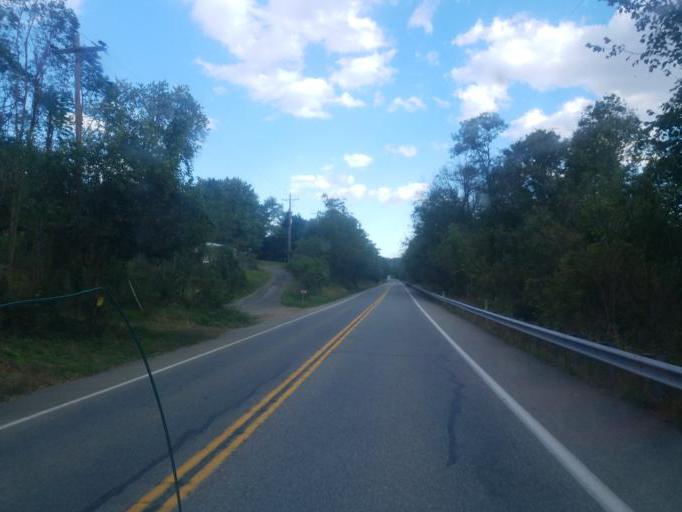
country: US
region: Pennsylvania
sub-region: Lancaster County
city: Bainbridge
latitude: 40.1197
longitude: -76.7057
